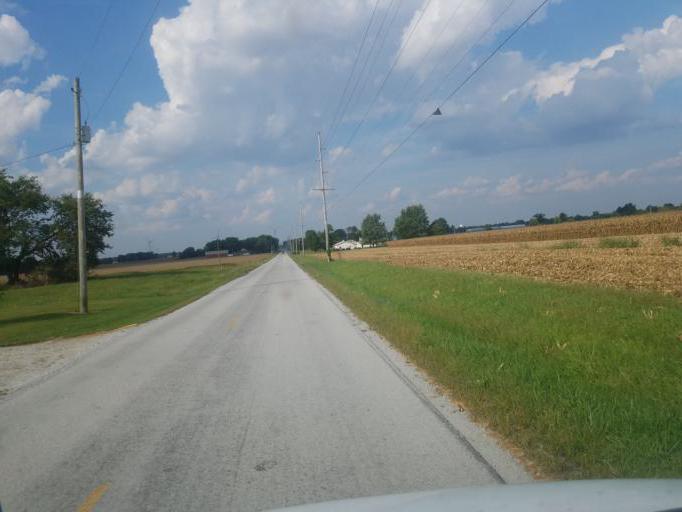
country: US
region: Ohio
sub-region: Hancock County
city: Arlington
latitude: 40.7728
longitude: -83.6521
